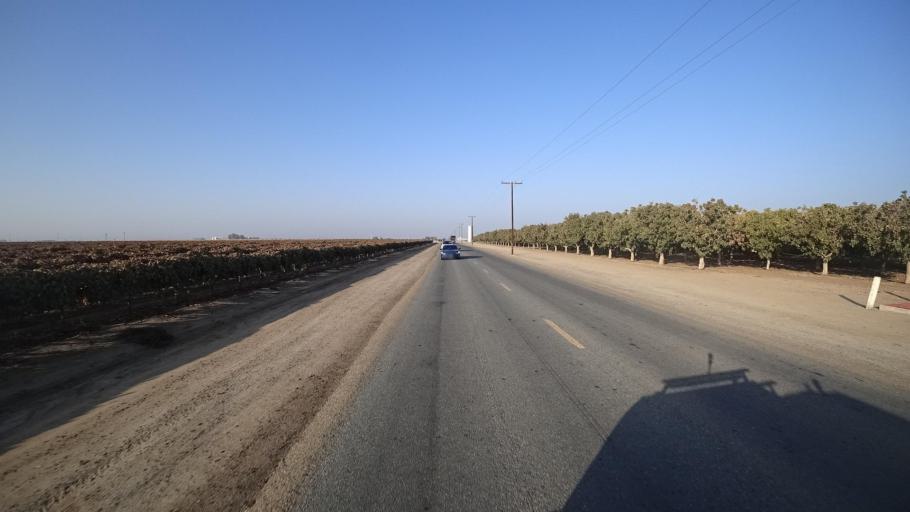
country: US
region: California
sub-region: Tulare County
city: Richgrove
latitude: 35.7905
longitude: -119.1748
